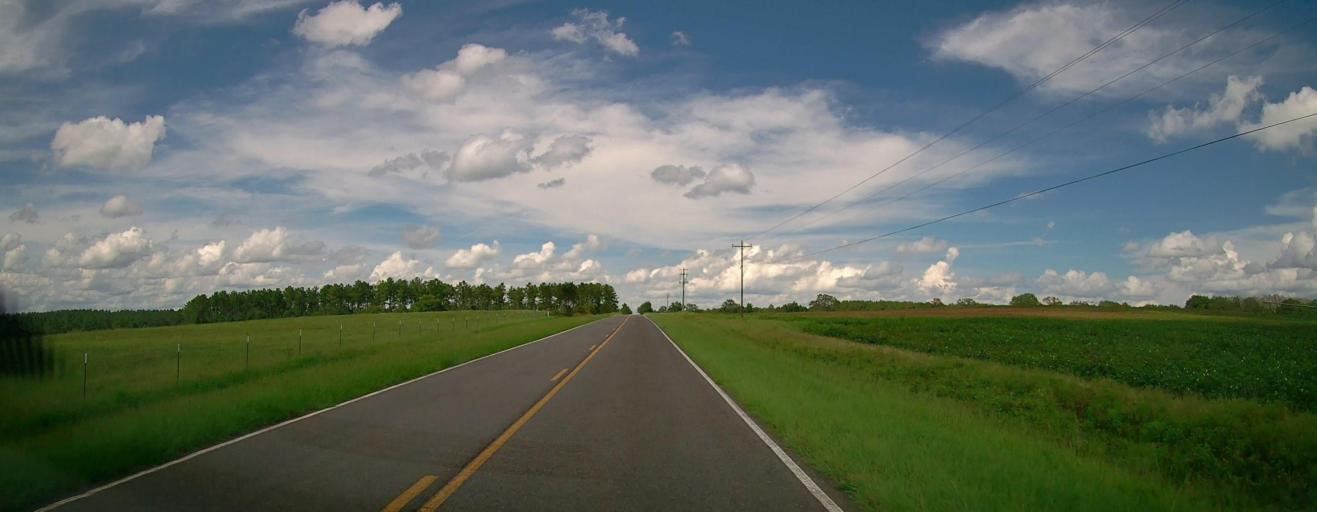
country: US
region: Georgia
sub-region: Taylor County
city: Butler
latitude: 32.4419
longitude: -84.1958
